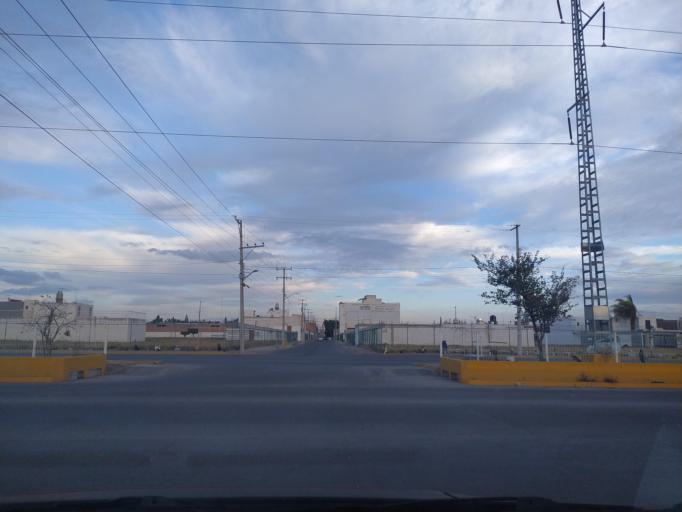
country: LA
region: Oudomxai
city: Muang La
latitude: 21.0189
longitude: 101.8699
